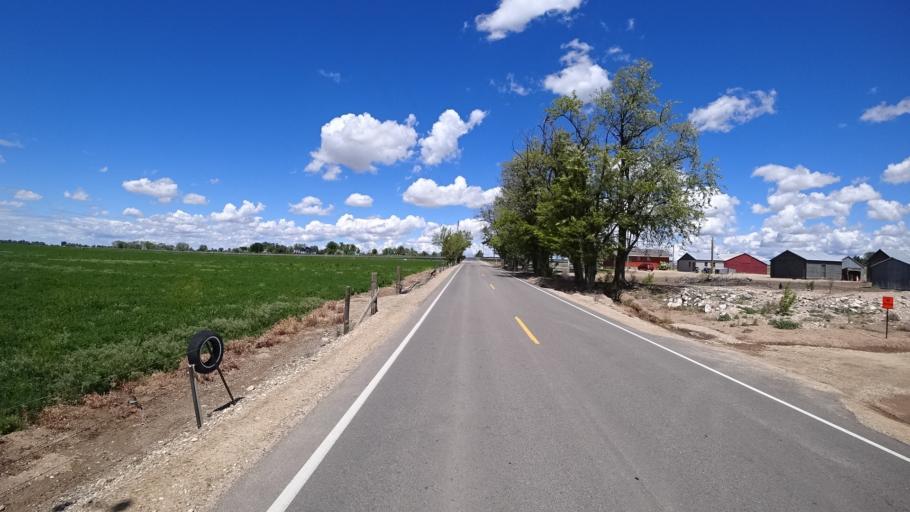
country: US
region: Idaho
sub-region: Ada County
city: Meridian
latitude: 43.5640
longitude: -116.4536
